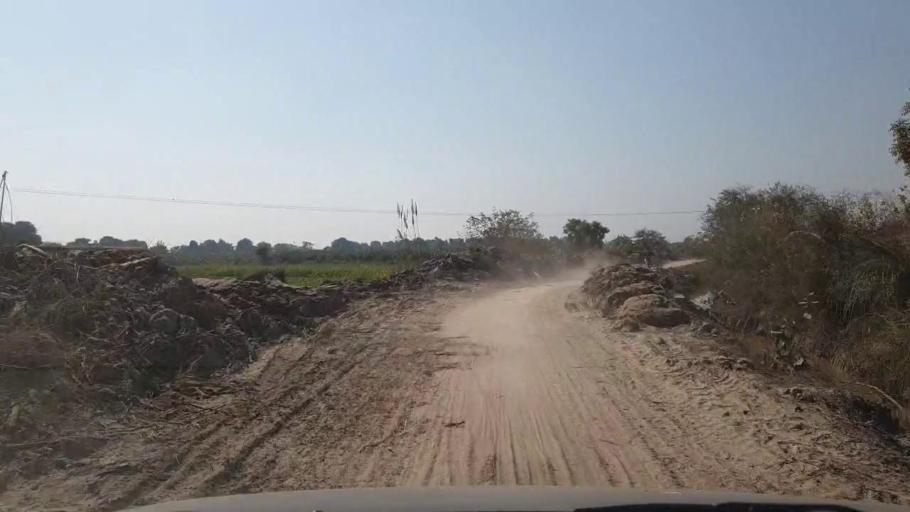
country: PK
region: Sindh
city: Tando Allahyar
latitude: 25.4328
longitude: 68.6408
